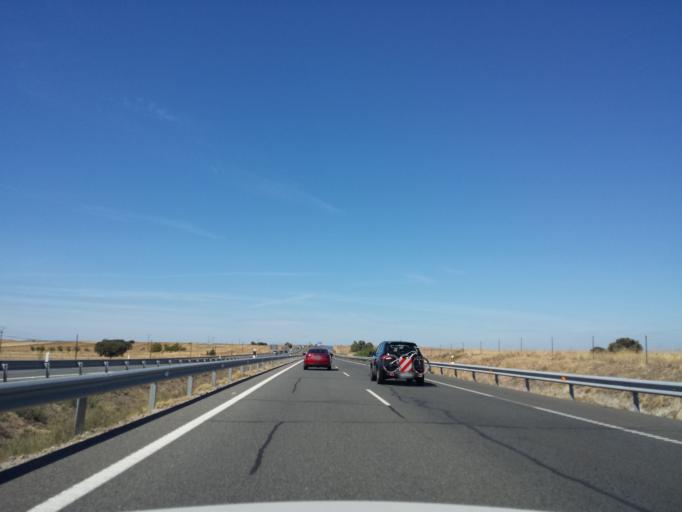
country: ES
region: Castille-La Mancha
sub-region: Province of Toledo
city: Lagartera
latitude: 39.9061
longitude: -5.2248
